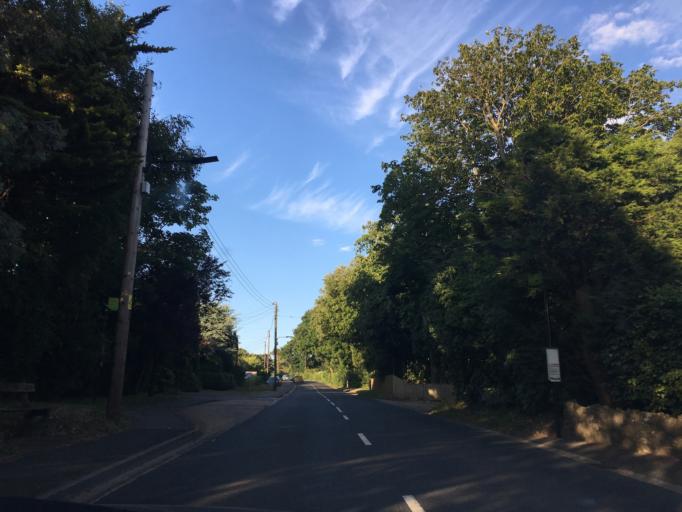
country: GB
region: England
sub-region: Isle of Wight
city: Newport
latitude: 50.7014
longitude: -1.2708
